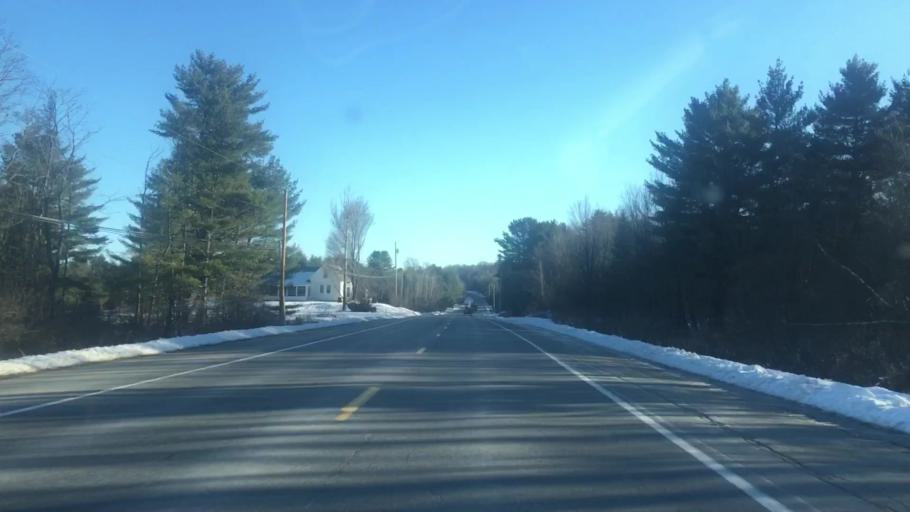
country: US
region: Maine
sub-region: Somerset County
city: Norridgewock
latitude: 44.6773
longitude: -69.7220
